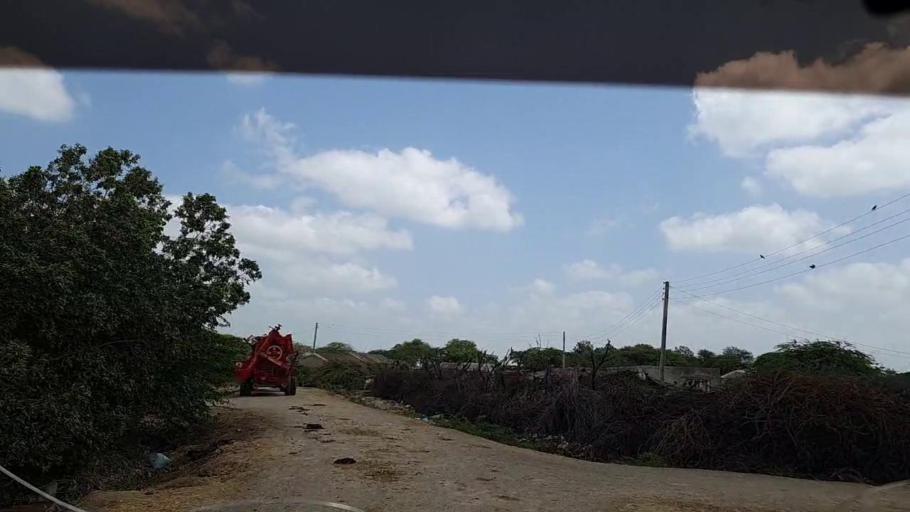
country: PK
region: Sindh
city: Badin
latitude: 24.5837
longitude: 68.7675
